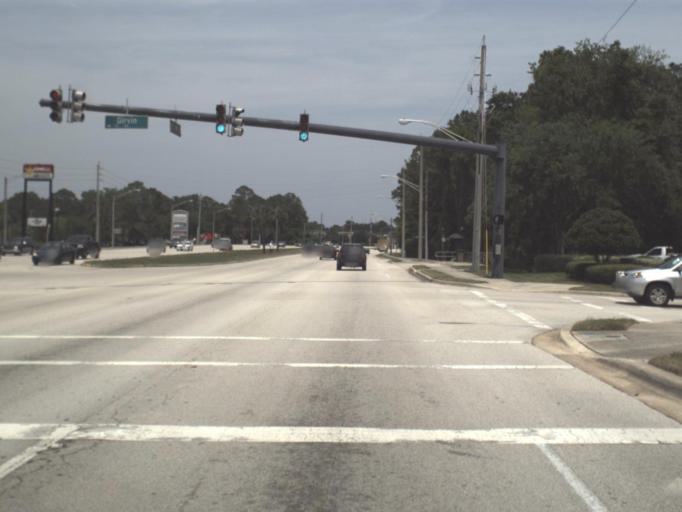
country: US
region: Florida
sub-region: Duval County
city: Atlantic Beach
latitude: 30.3181
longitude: -81.4731
